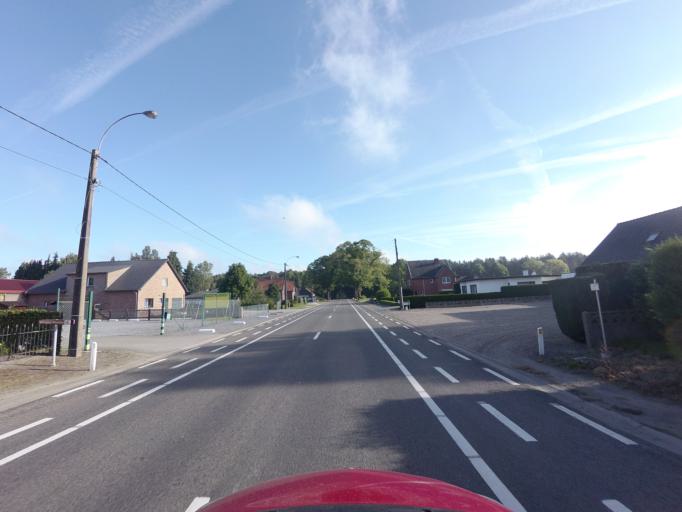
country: BE
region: Flanders
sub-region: Provincie Limburg
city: Overpelt
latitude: 51.1648
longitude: 5.3645
